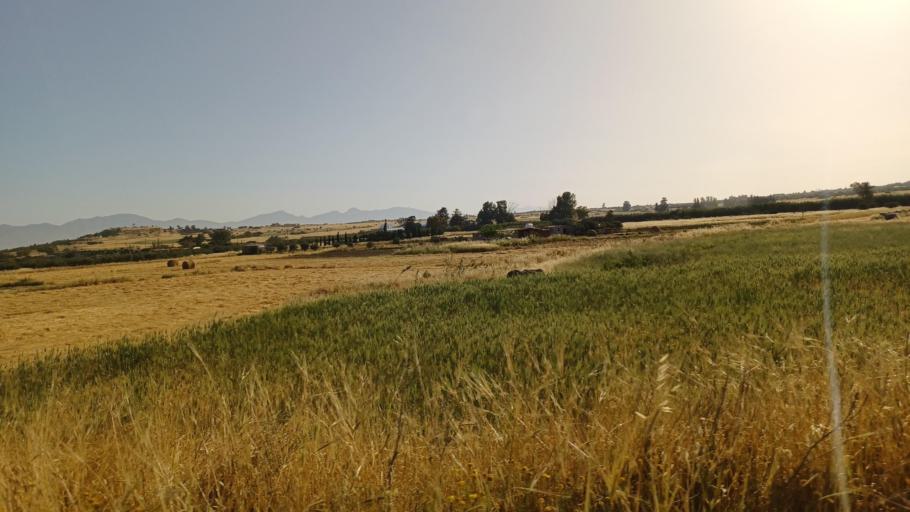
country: CY
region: Lefkosia
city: Mammari
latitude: 35.1627
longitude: 33.2465
